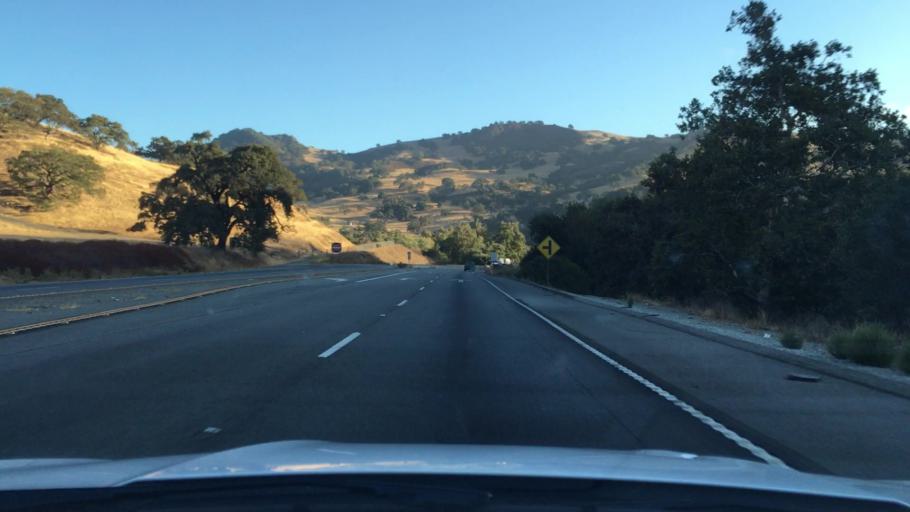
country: US
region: California
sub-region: San Benito County
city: Hollister
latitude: 37.0422
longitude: -121.2907
